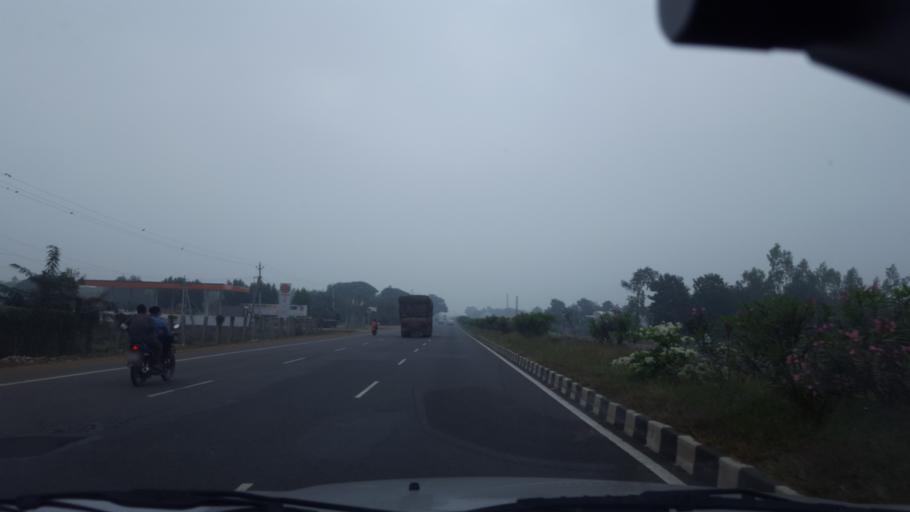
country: IN
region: Andhra Pradesh
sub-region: Prakasam
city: Ongole
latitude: 15.6045
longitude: 80.0287
